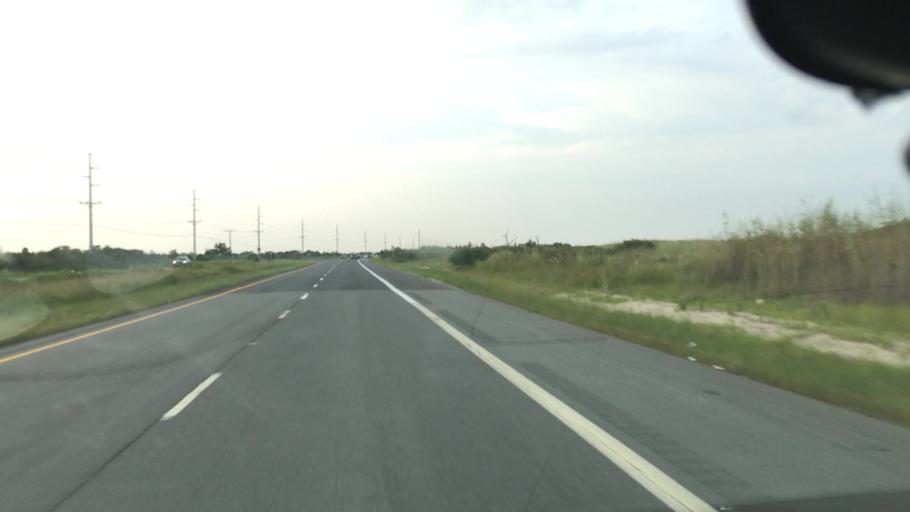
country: US
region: Delaware
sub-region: Sussex County
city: Ocean View
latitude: 38.6247
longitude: -75.0665
